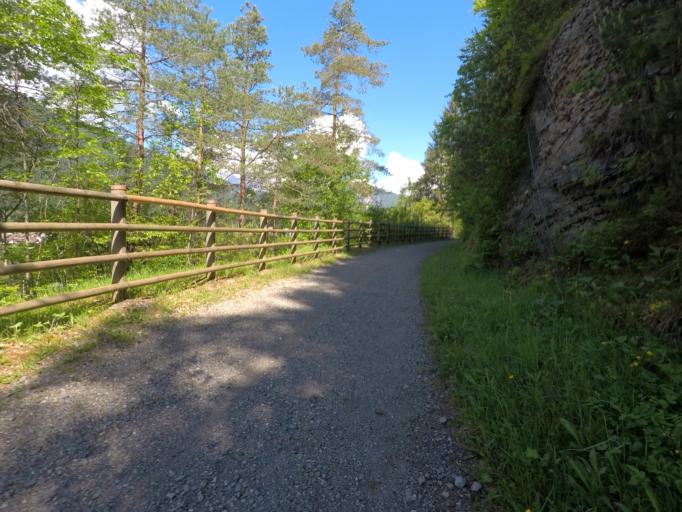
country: IT
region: Friuli Venezia Giulia
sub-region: Provincia di Udine
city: Ovaro
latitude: 46.4757
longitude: 12.8712
